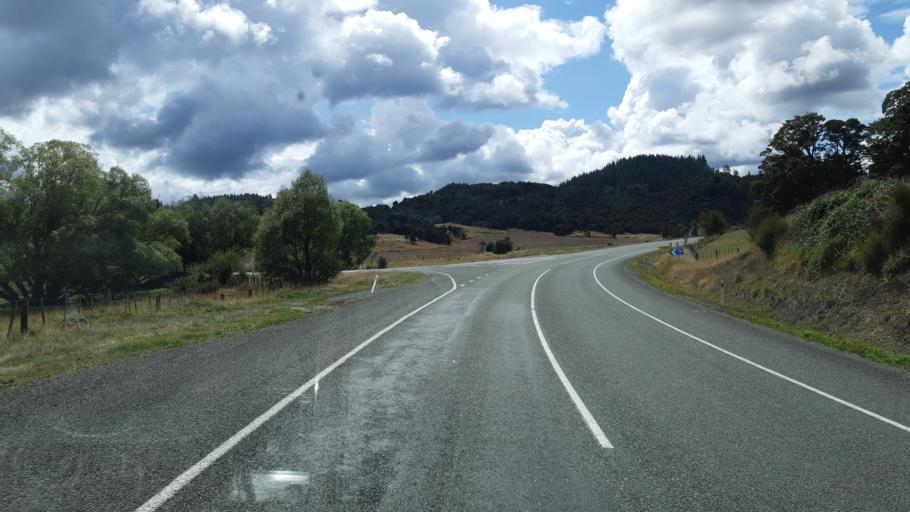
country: NZ
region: Tasman
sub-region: Tasman District
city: Wakefield
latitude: -41.6434
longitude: 172.6599
